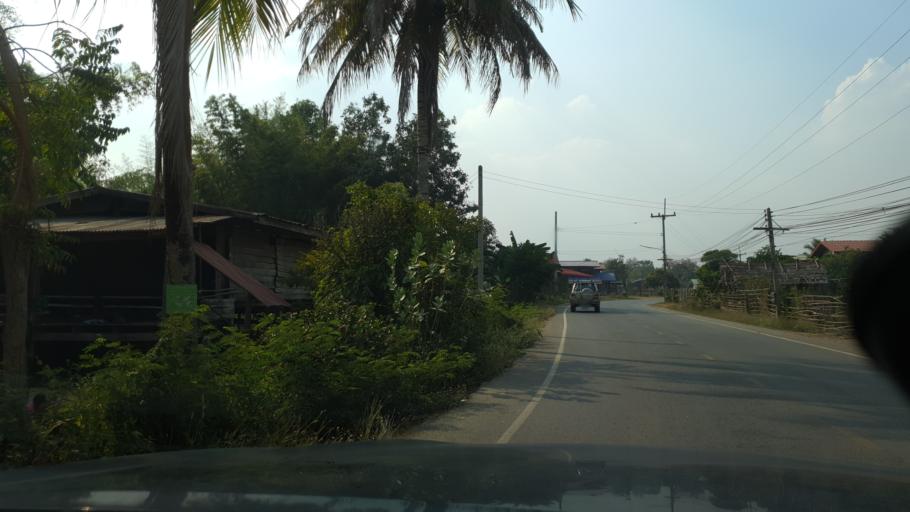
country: TH
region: Sukhothai
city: Ban Dan Lan Hoi
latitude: 17.1163
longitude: 99.5380
